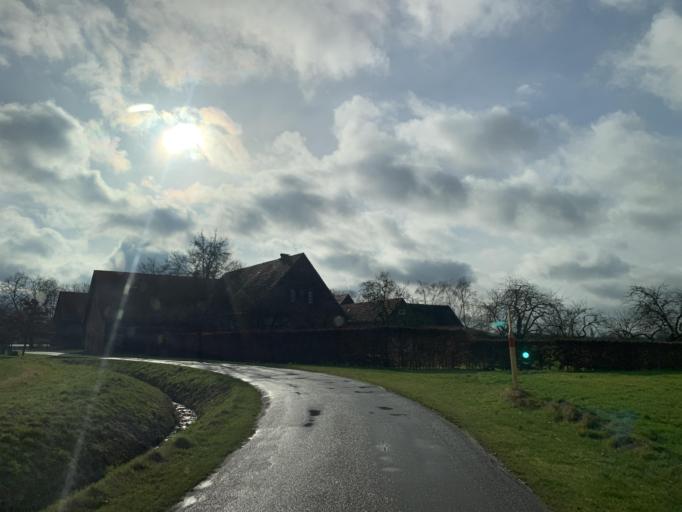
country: DE
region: North Rhine-Westphalia
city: Ludinghausen
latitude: 51.7891
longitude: 7.4600
